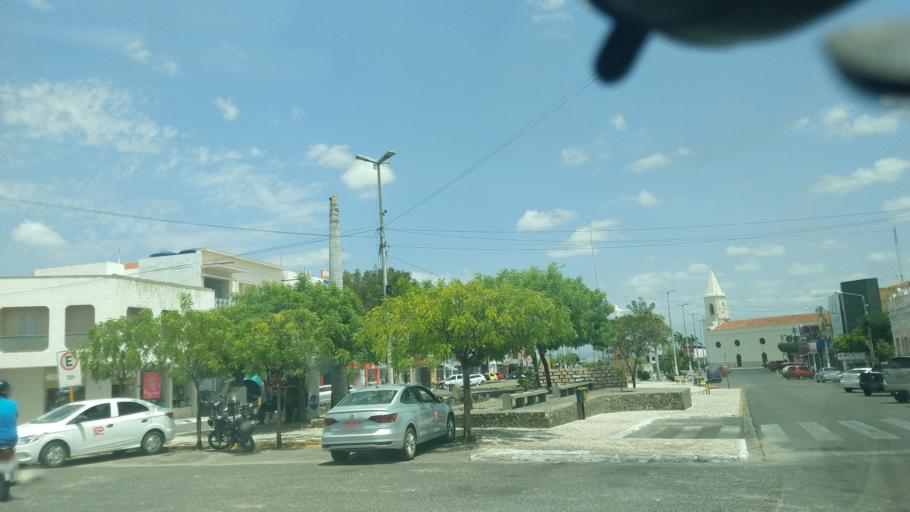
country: BR
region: Rio Grande do Norte
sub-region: Currais Novos
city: Currais Novos
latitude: -6.2636
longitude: -36.5158
